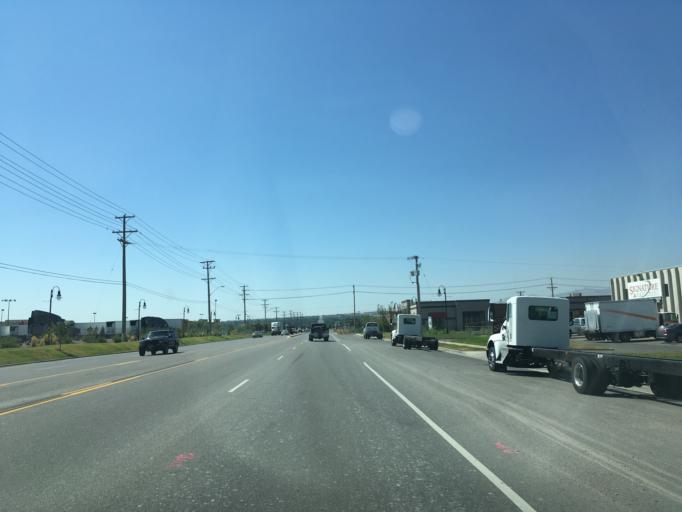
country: US
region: Utah
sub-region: Salt Lake County
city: West Valley City
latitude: 40.7166
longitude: -112.0250
